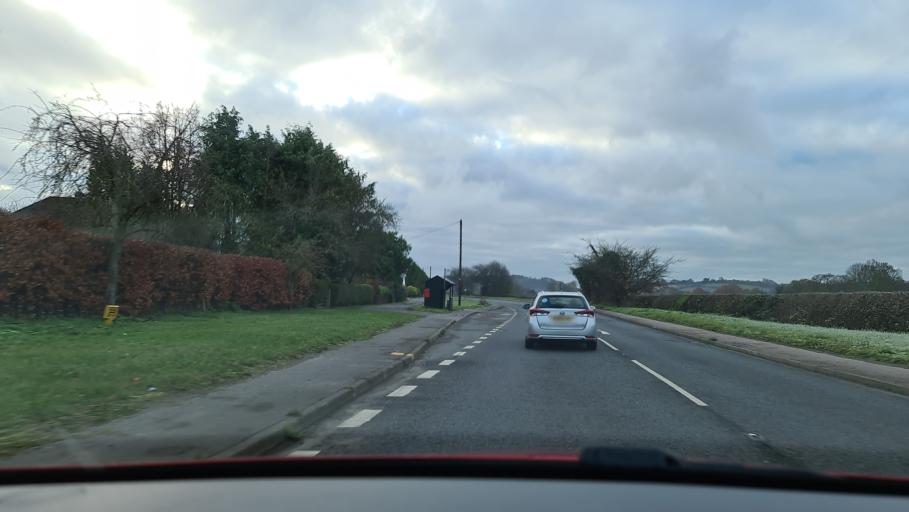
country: GB
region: England
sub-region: Buckinghamshire
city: Princes Risborough
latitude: 51.6892
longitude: -0.8320
